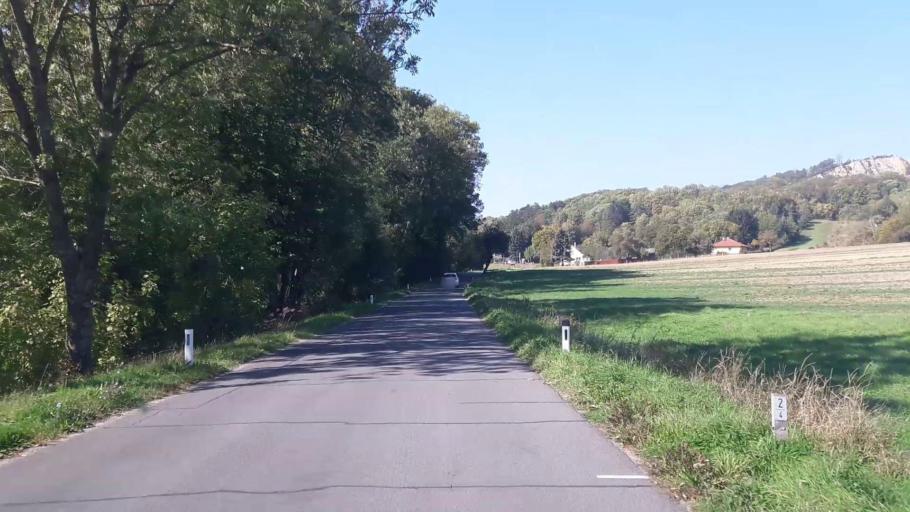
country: AT
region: Lower Austria
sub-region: Politischer Bezirk Korneuburg
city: Ernstbrunn
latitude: 48.5388
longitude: 16.3618
